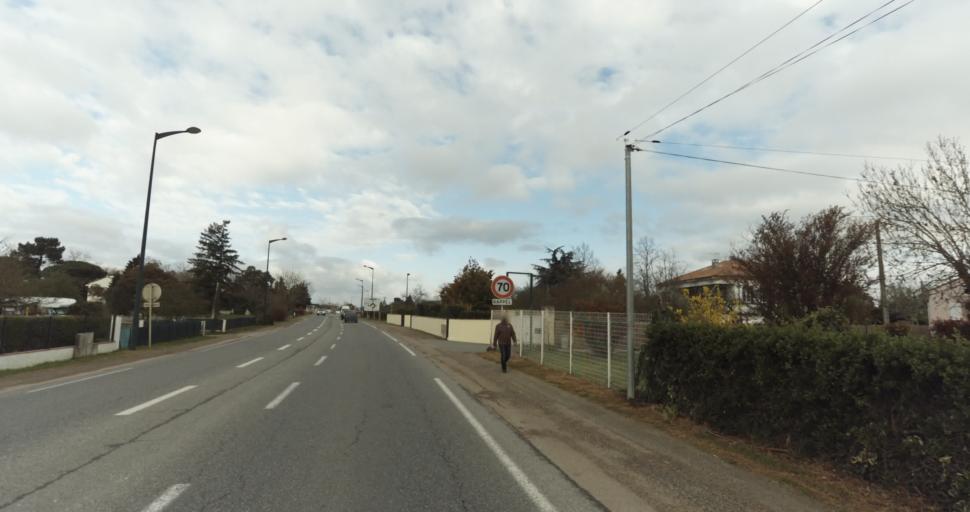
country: FR
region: Midi-Pyrenees
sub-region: Departement de la Haute-Garonne
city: Auterive
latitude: 43.3656
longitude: 1.4546
